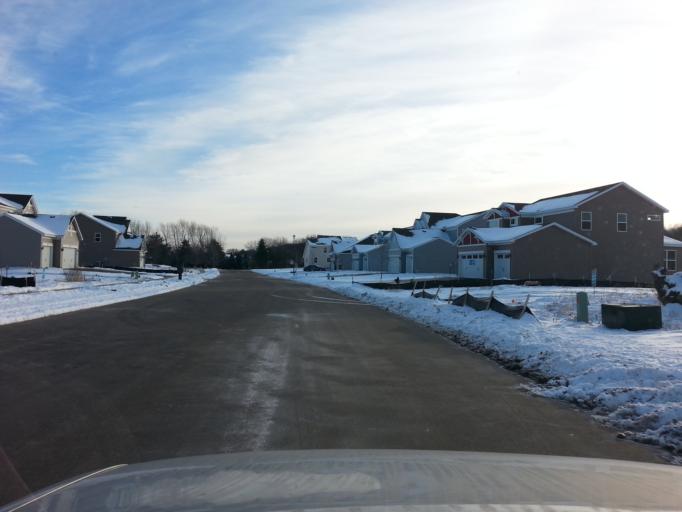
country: US
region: Minnesota
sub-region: Scott County
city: Prior Lake
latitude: 44.7656
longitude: -93.4170
